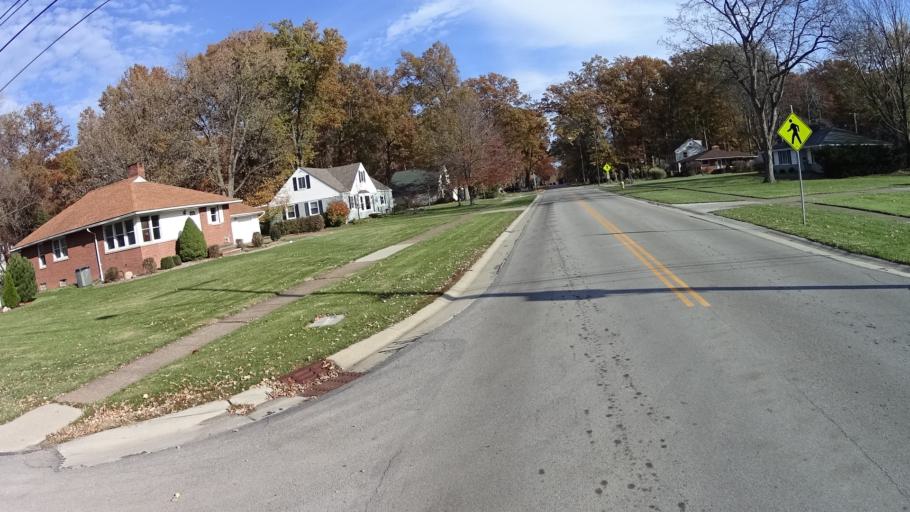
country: US
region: Ohio
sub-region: Lorain County
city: Avon Lake
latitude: 41.5026
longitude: -82.0385
